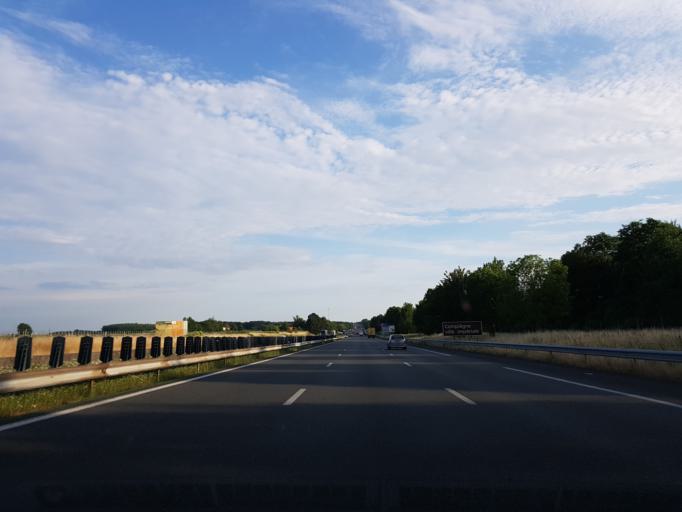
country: FR
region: Picardie
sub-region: Departement de l'Oise
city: Ressons-sur-Matz
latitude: 49.5484
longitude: 2.7300
